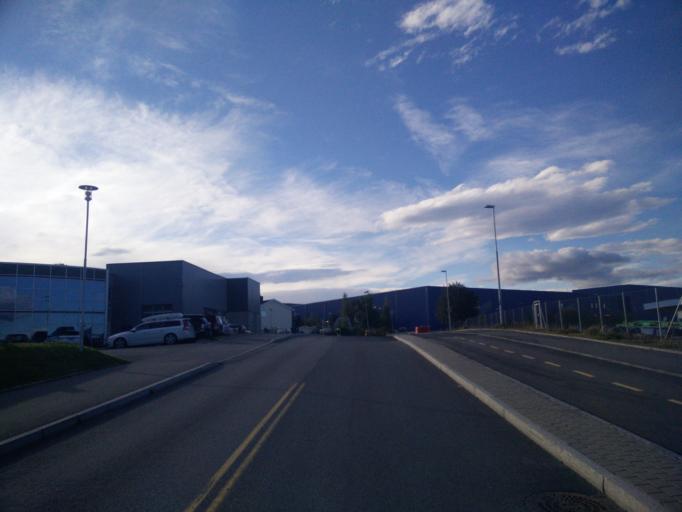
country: NO
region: Sor-Trondelag
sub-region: Trondheim
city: Trondheim
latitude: 63.4310
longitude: 10.4733
